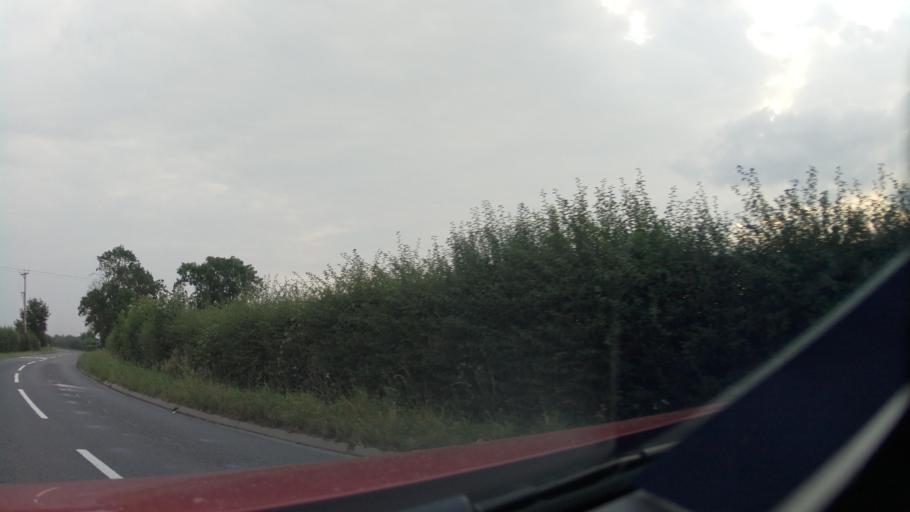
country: GB
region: England
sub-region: Lincolnshire
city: Skellingthorpe
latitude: 53.1355
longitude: -0.6459
